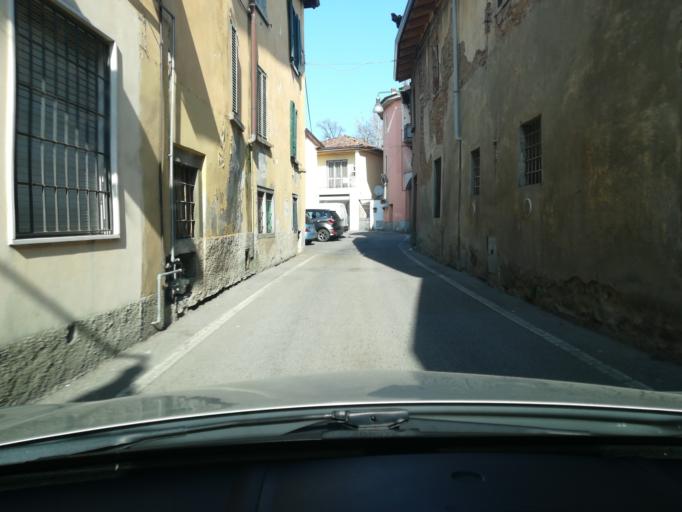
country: IT
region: Lombardy
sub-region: Provincia di Bergamo
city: Stezzano
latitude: 45.6499
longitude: 9.6553
